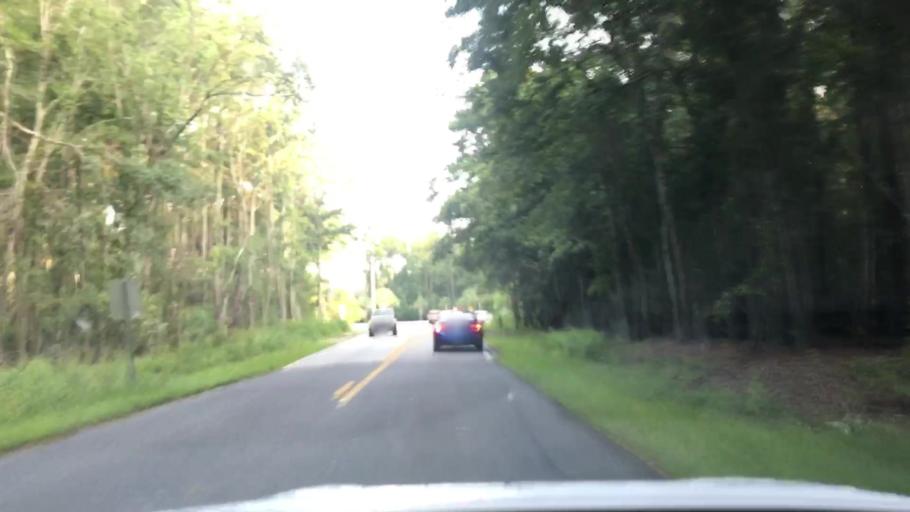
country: US
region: South Carolina
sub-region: Charleston County
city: Shell Point
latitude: 32.8187
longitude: -80.0917
